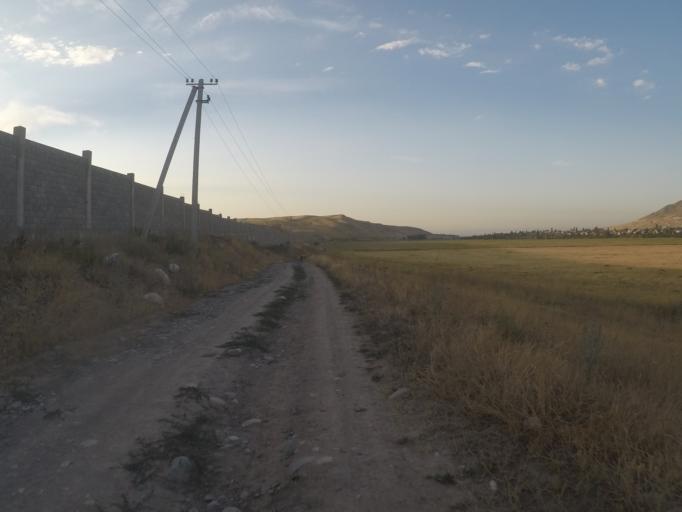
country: KG
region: Chuy
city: Bishkek
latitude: 42.7524
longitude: 74.6368
